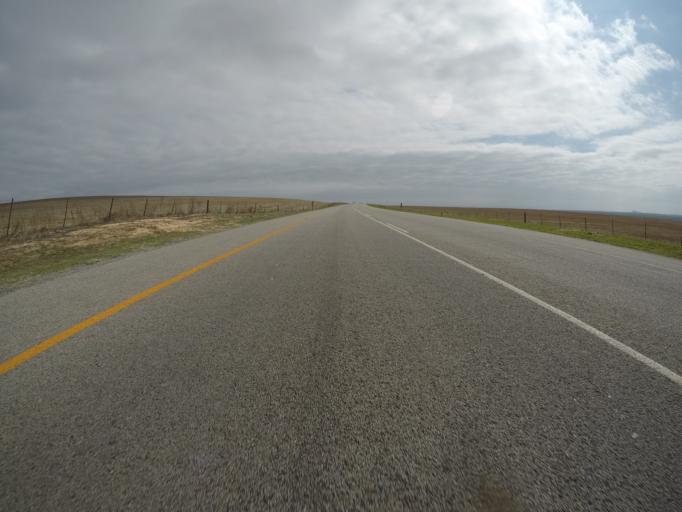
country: ZA
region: Western Cape
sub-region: City of Cape Town
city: Sunset Beach
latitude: -33.7238
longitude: 18.5002
